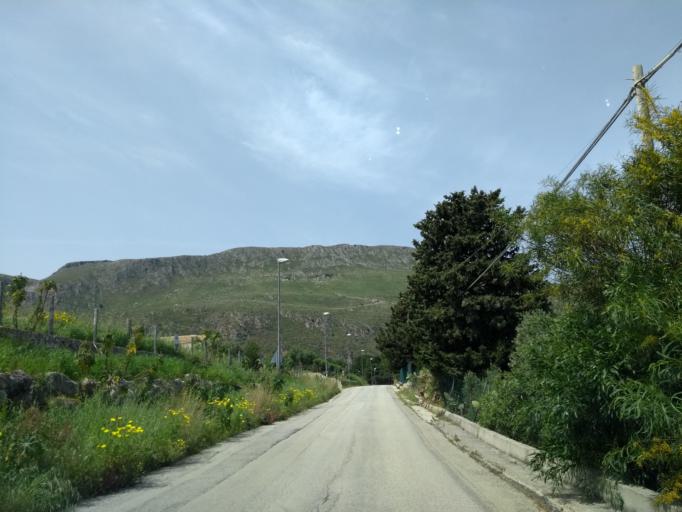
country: IT
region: Sicily
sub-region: Trapani
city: Castelluzzo
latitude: 38.0742
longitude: 12.8154
